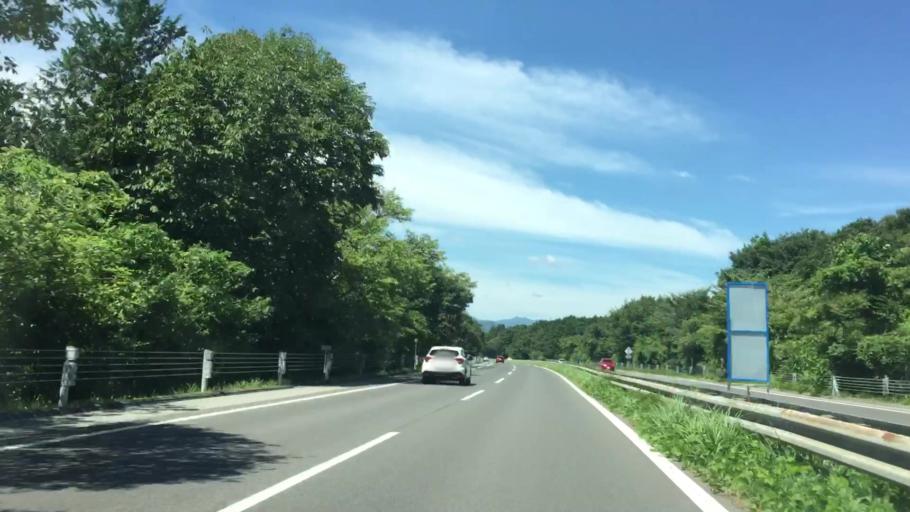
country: JP
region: Tochigi
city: Imaichi
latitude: 36.6741
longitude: 139.7938
